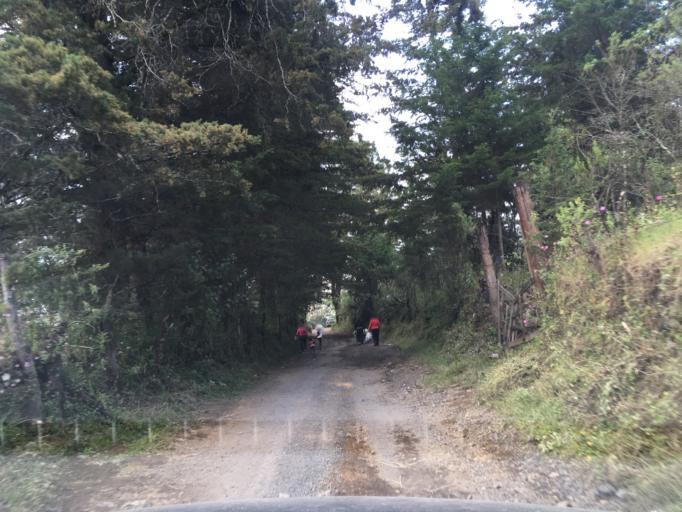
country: MX
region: Michoacan
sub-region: Uruapan
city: Santa Ana Zirosto
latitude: 19.5700
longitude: -102.2886
